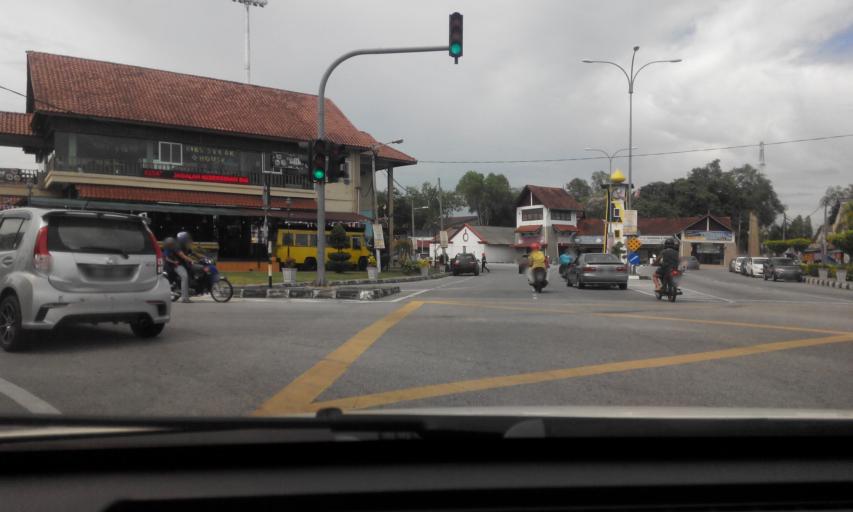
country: MY
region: Perak
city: Parit Buntar
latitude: 5.1295
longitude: 100.4906
